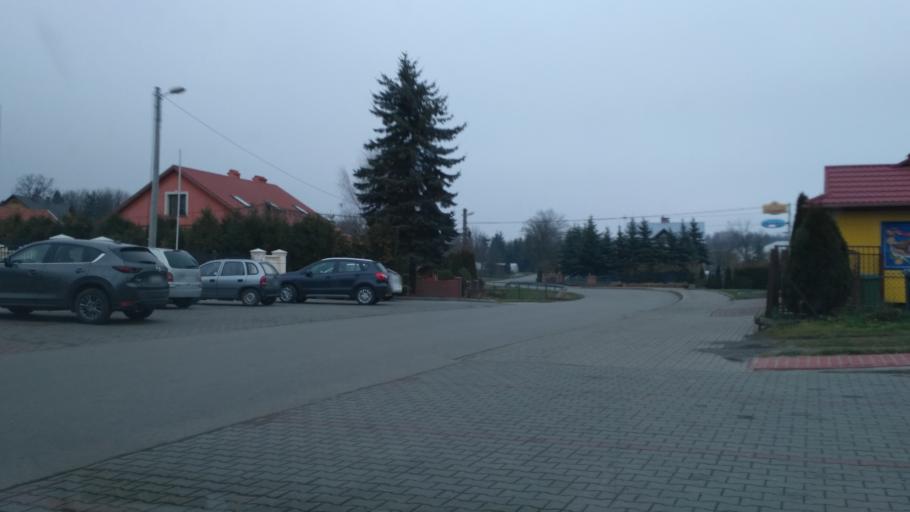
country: PL
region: Subcarpathian Voivodeship
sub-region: Powiat jaroslawski
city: Pawlosiow
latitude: 49.9936
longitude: 22.6439
